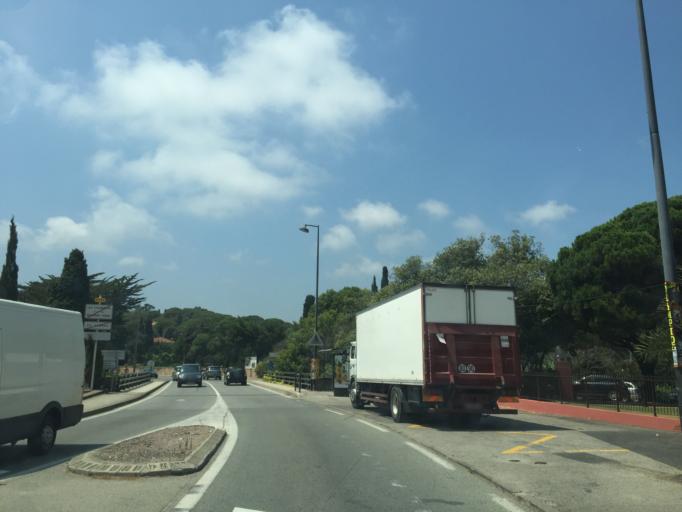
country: FR
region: Provence-Alpes-Cote d'Azur
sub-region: Departement du Var
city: Sainte-Maxime
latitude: 43.3415
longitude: 6.6829
